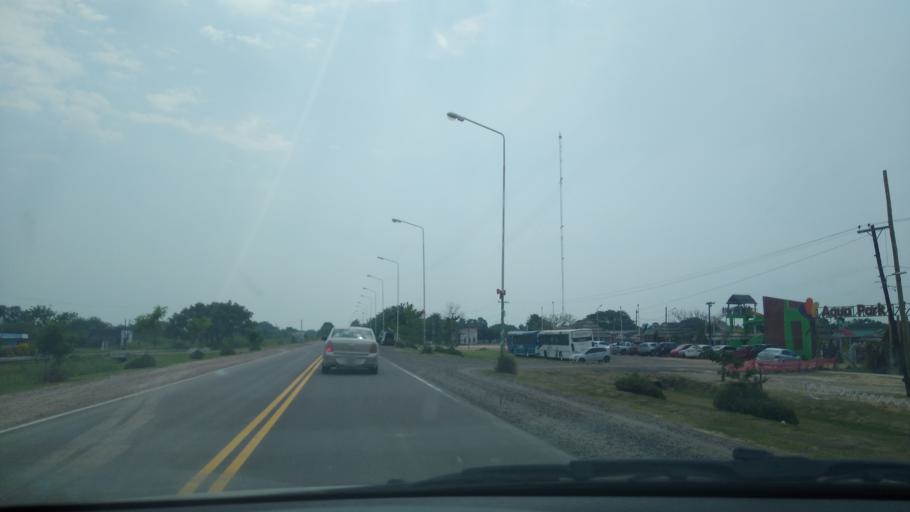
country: AR
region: Chaco
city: La Eduvigis
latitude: -26.8360
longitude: -59.0660
